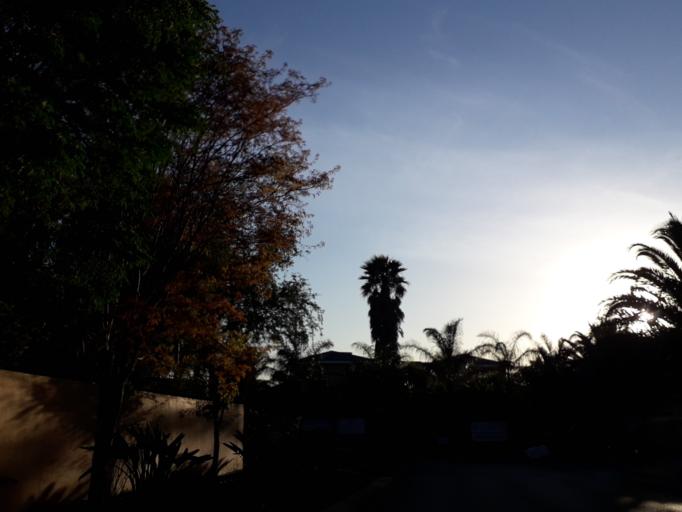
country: ZA
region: Gauteng
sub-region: City of Johannesburg Metropolitan Municipality
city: Roodepoort
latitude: -26.1576
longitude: 27.9522
